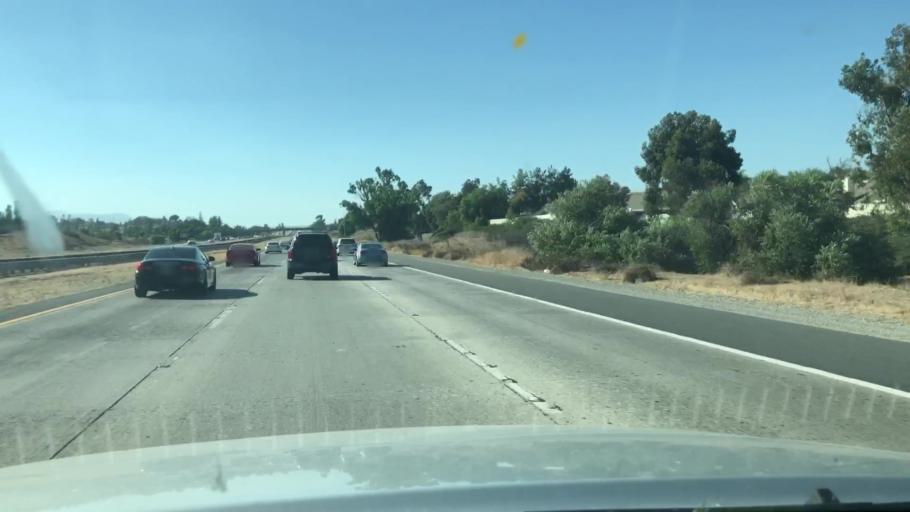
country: US
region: California
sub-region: Riverside County
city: Murrieta
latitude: 33.5729
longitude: -117.2164
